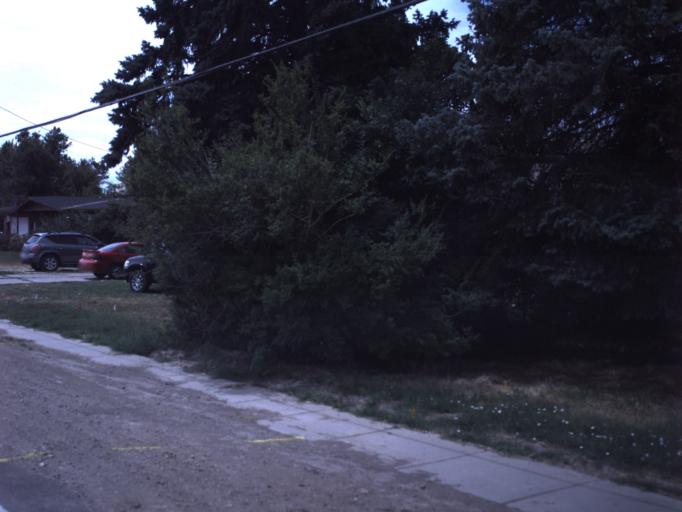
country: US
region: Utah
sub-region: Davis County
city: Syracuse
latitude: 41.1067
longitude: -112.0646
